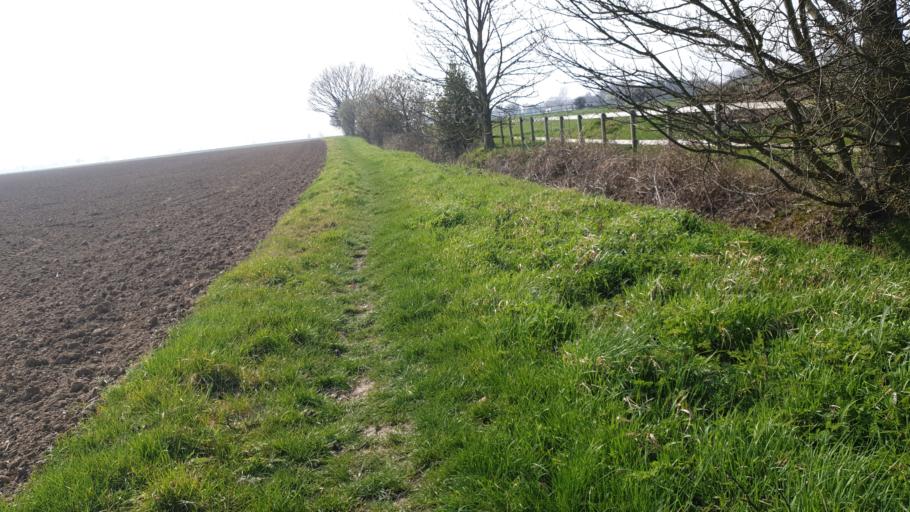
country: GB
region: England
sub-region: Essex
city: Mistley
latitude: 51.9090
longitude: 1.1353
